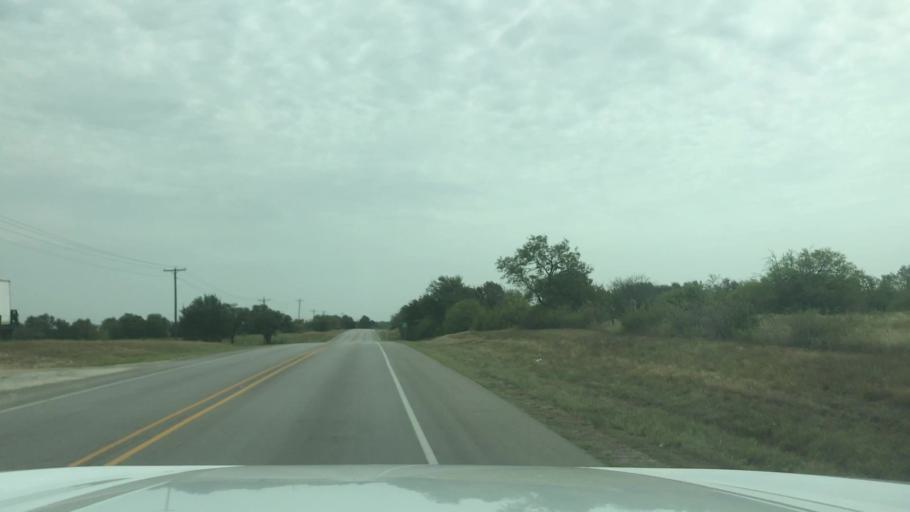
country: US
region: Texas
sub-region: Erath County
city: Dublin
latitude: 32.0938
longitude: -98.4135
